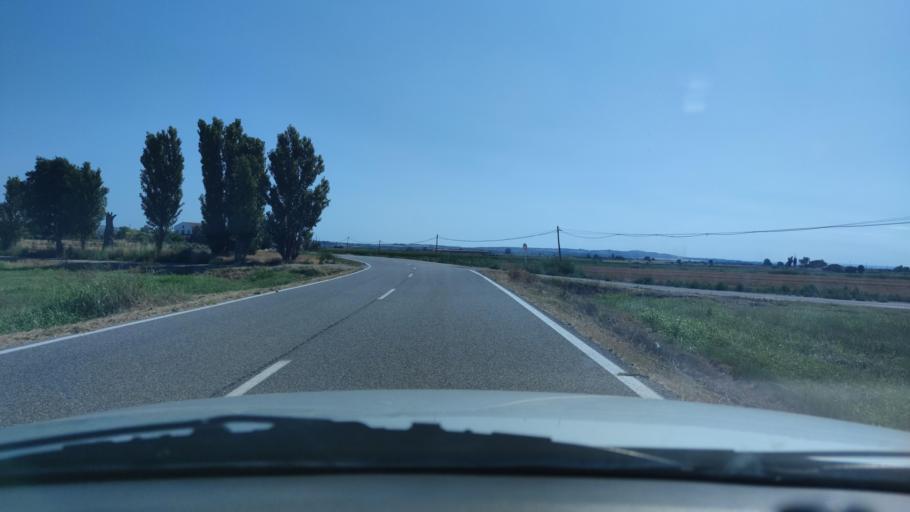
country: ES
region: Catalonia
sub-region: Provincia de Lleida
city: Penelles
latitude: 41.7377
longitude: 0.9442
